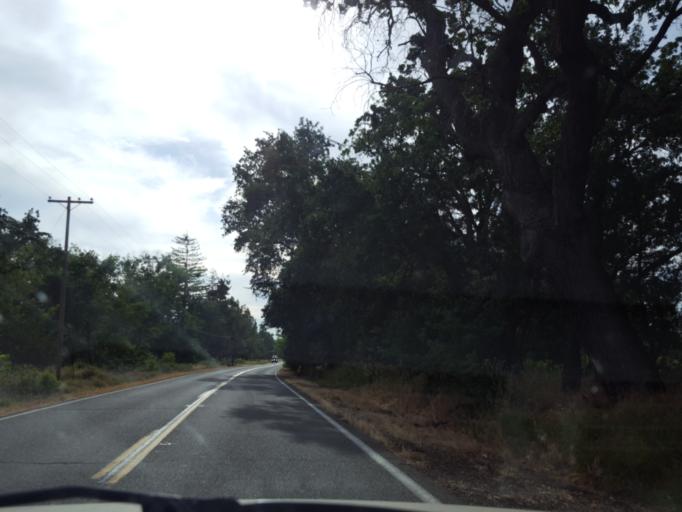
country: US
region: California
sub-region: Merced County
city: Merced
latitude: 37.5224
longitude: -120.4157
